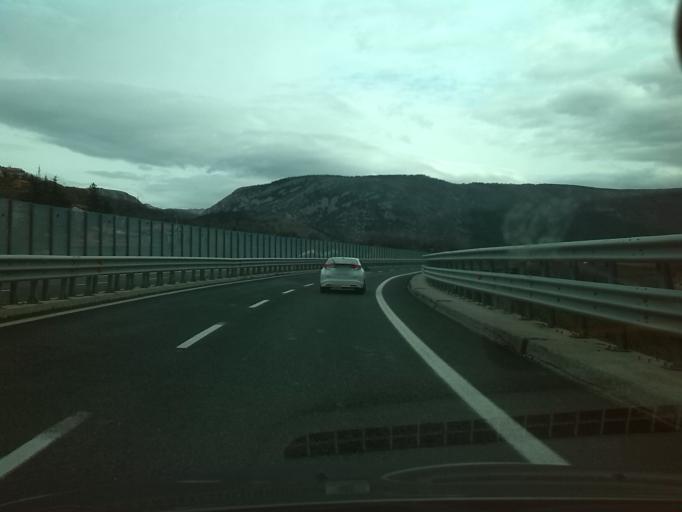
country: IT
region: Friuli Venezia Giulia
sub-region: Provincia di Trieste
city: Domio
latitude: 45.6249
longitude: 13.8364
